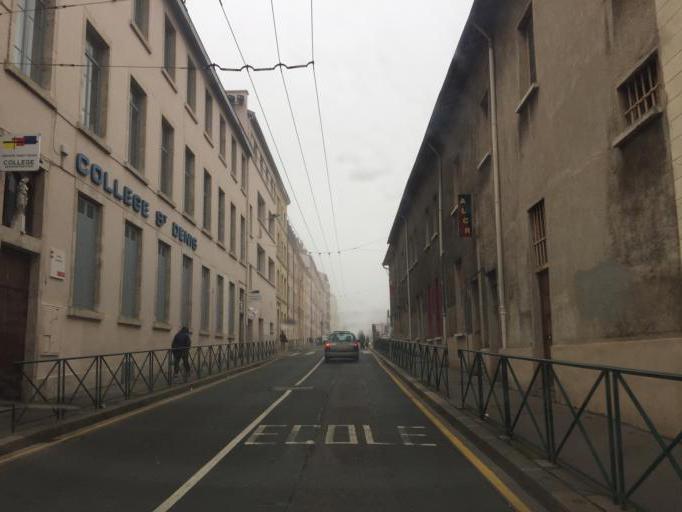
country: FR
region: Rhone-Alpes
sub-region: Departement du Rhone
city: Caluire-et-Cuire
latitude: 45.7795
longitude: 4.8318
